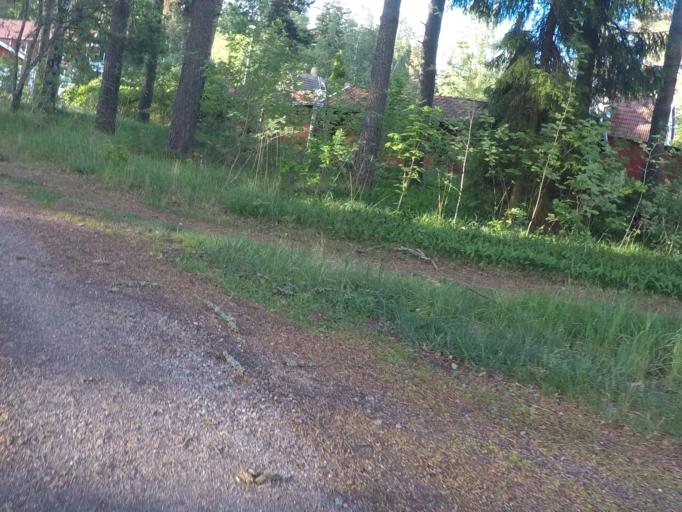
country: SE
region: Soedermanland
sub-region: Eskilstuna Kommun
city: Hallbybrunn
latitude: 59.3924
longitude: 16.4064
